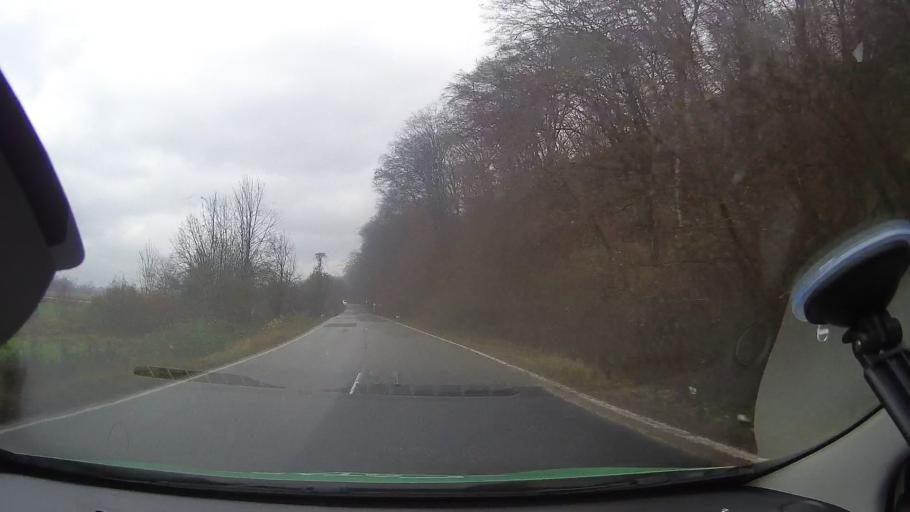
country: RO
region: Arad
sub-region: Comuna Buteni
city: Buteni
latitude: 46.3000
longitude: 22.1653
